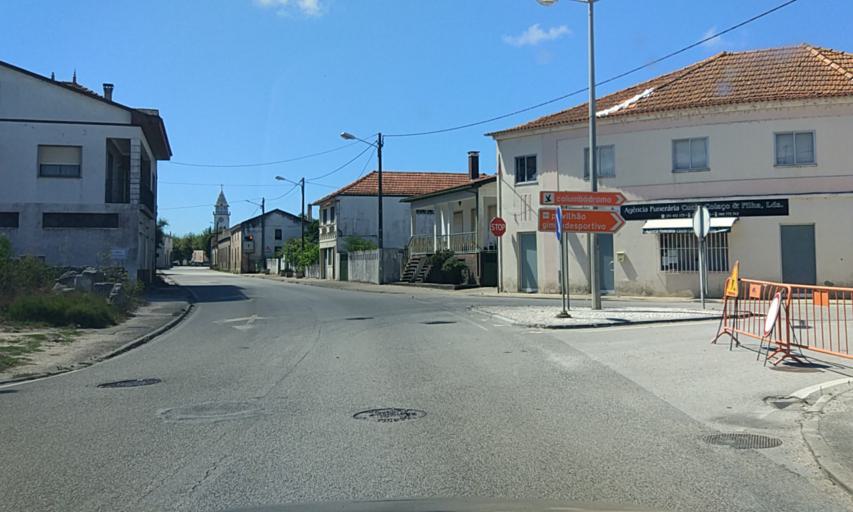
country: PT
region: Coimbra
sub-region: Mira
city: Mira
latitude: 40.4449
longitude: -8.7251
